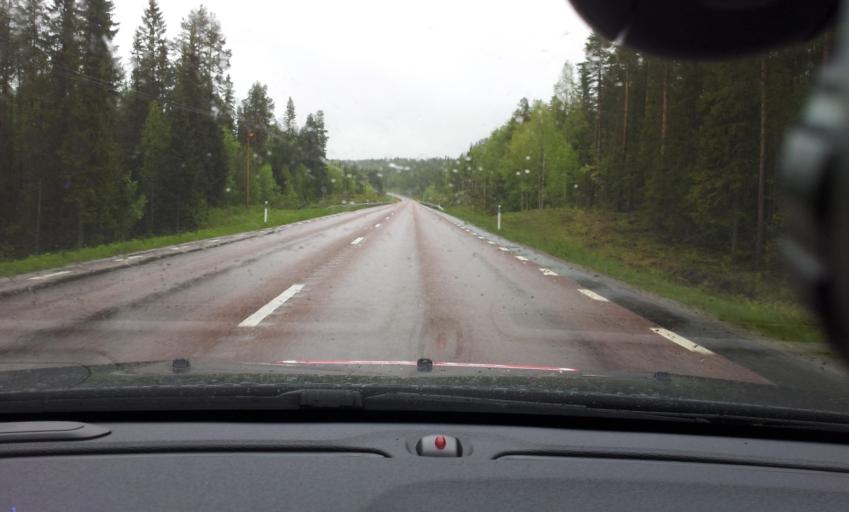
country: SE
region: Jaemtland
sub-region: Bergs Kommun
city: Hoverberg
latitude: 62.8667
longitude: 14.5200
